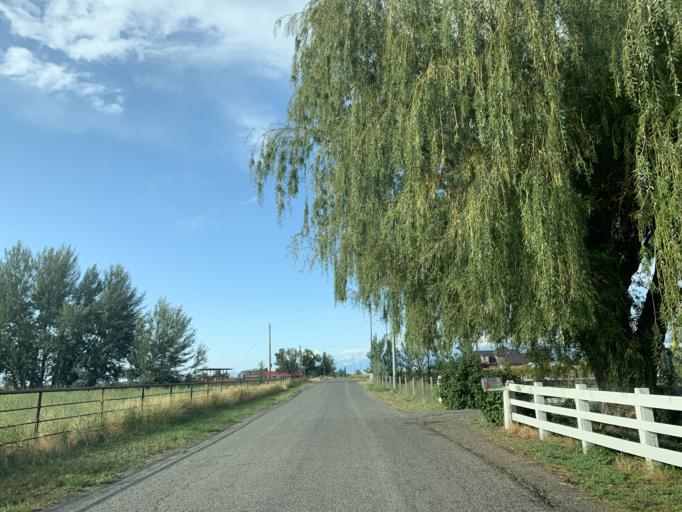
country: US
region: Utah
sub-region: Utah County
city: Benjamin
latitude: 40.1207
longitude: -111.7691
